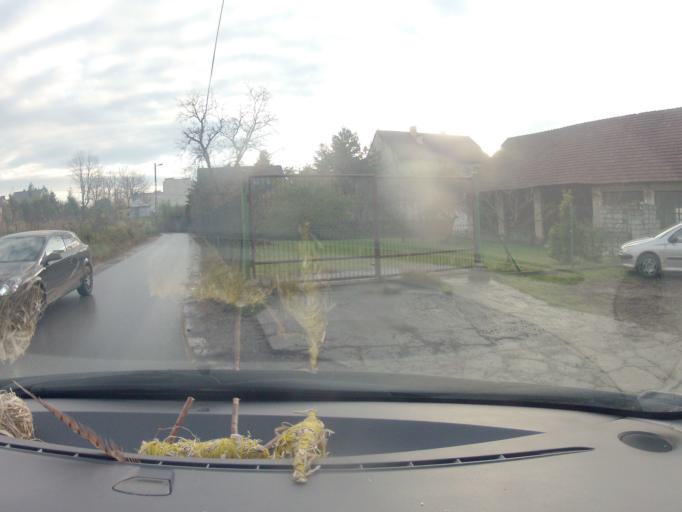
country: PL
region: Lesser Poland Voivodeship
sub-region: Krakow
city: Sidzina
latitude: 50.0076
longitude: 19.8898
